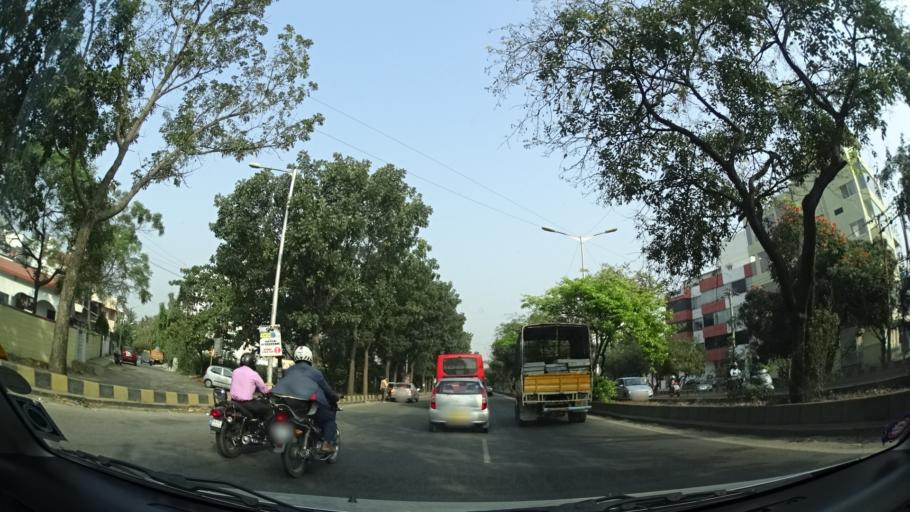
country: IN
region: Karnataka
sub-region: Bangalore Urban
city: Bangalore
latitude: 13.0314
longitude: 77.6302
